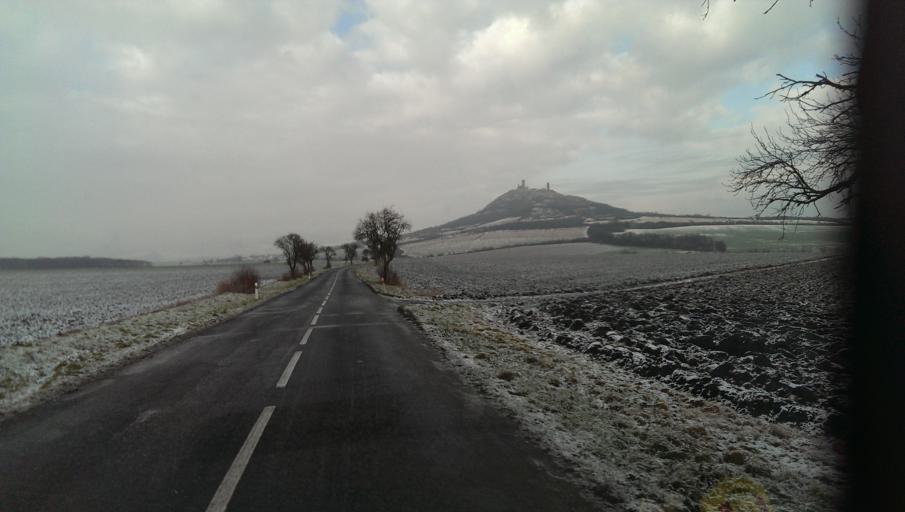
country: CZ
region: Ustecky
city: Libochovice
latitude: 50.4143
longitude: 14.0284
